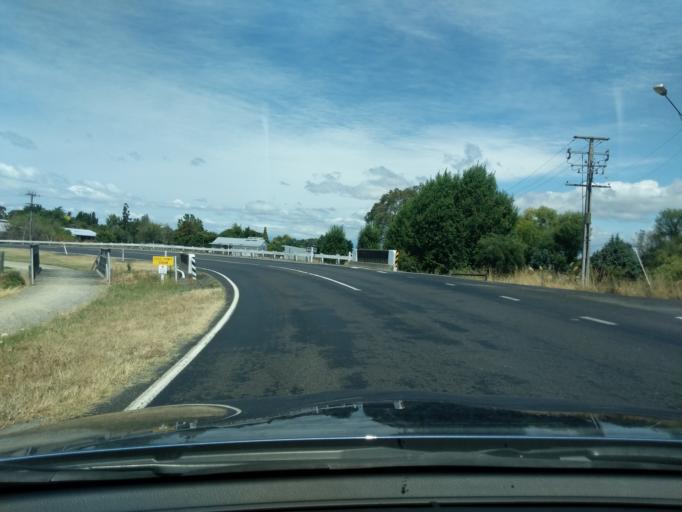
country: NZ
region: Tasman
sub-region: Tasman District
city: Motueka
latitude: -41.0754
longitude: 172.9952
